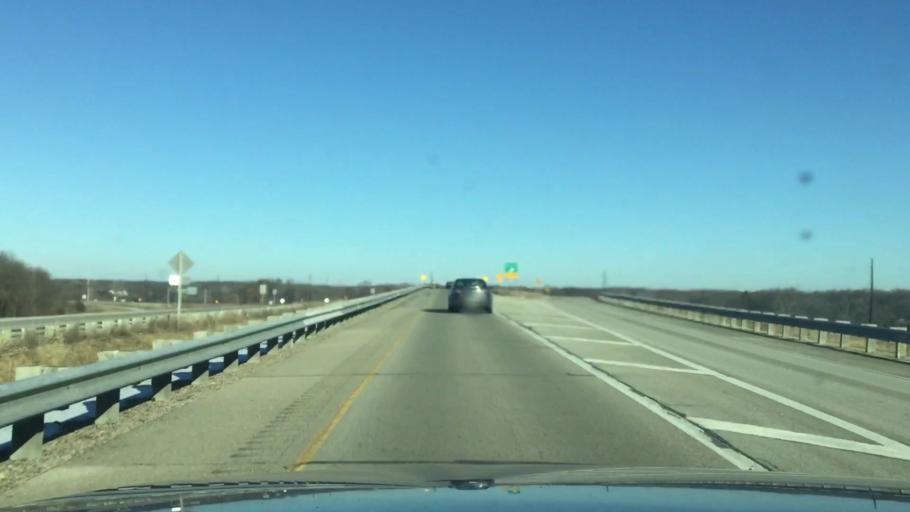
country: US
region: Wisconsin
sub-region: Racine County
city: Browns Lake
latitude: 42.7147
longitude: -88.2294
